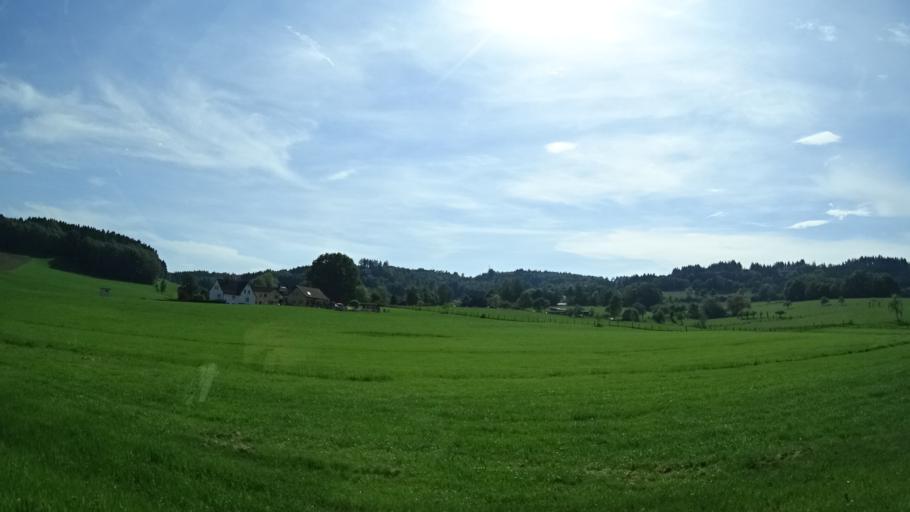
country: DE
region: Hesse
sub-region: Regierungsbezirk Darmstadt
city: Wald-Michelbach
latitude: 49.6157
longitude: 8.8334
